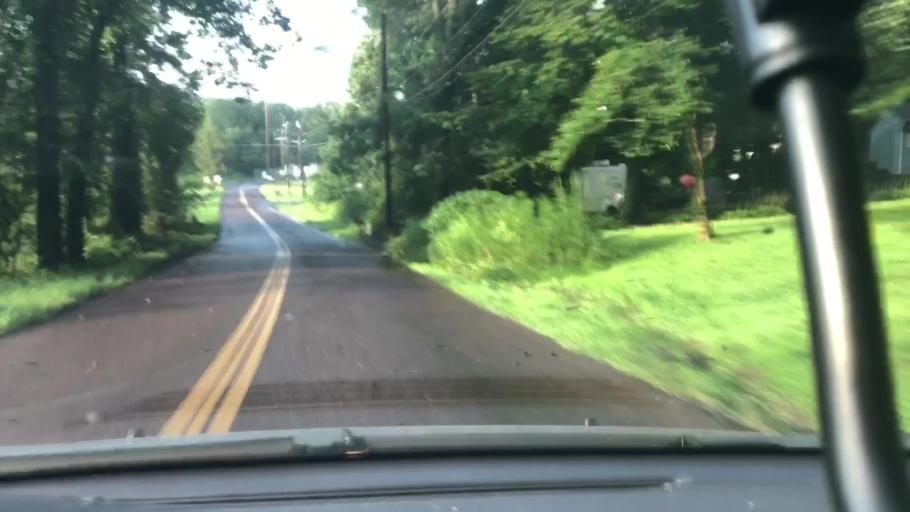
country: US
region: Pennsylvania
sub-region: Chester County
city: Kenilworth
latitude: 40.1920
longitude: -75.6467
